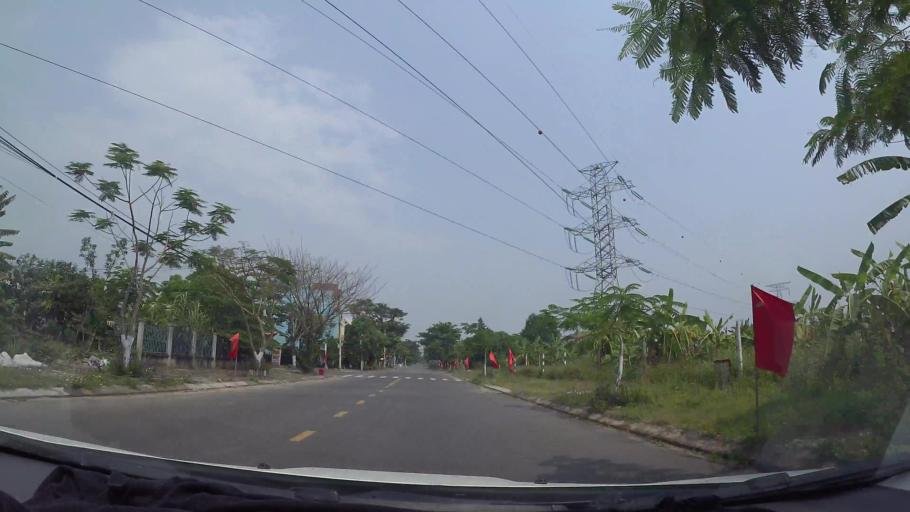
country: VN
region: Da Nang
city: Cam Le
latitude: 16.0011
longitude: 108.2104
